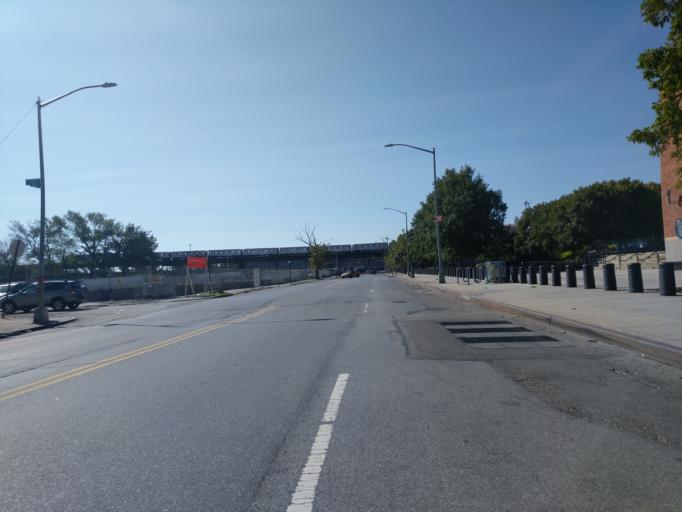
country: US
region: New York
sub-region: Queens County
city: Borough of Queens
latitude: 40.7572
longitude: -73.8443
